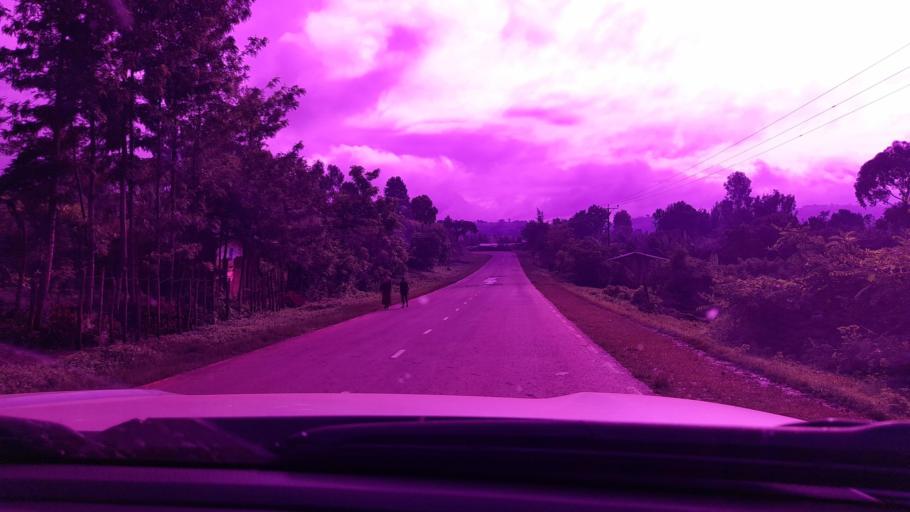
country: ET
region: Oromiya
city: Bedele
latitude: 8.2267
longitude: 36.4493
